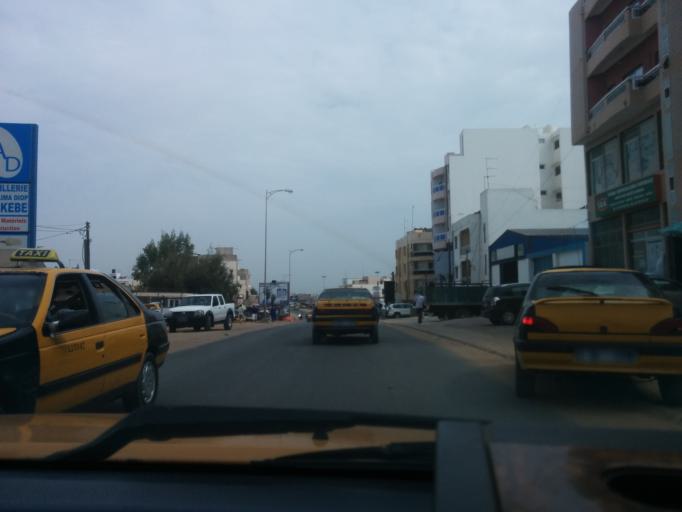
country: SN
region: Dakar
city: Grand Dakar
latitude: 14.7518
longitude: -17.4542
